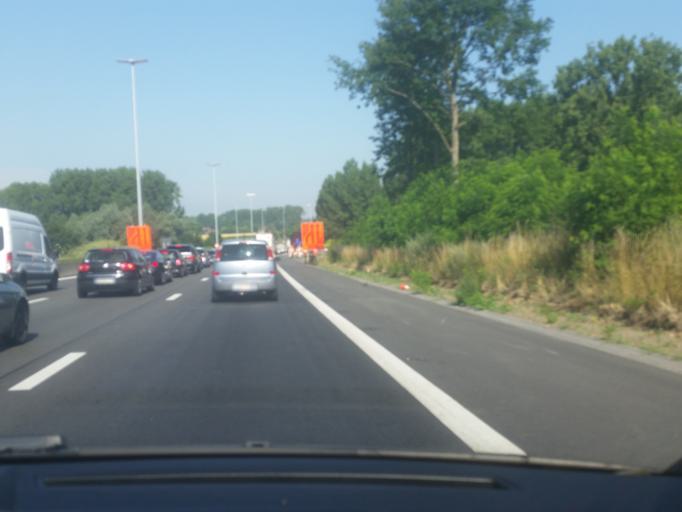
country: BE
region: Flanders
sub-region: Provincie Oost-Vlaanderen
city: Lede
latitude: 50.9304
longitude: 3.9423
